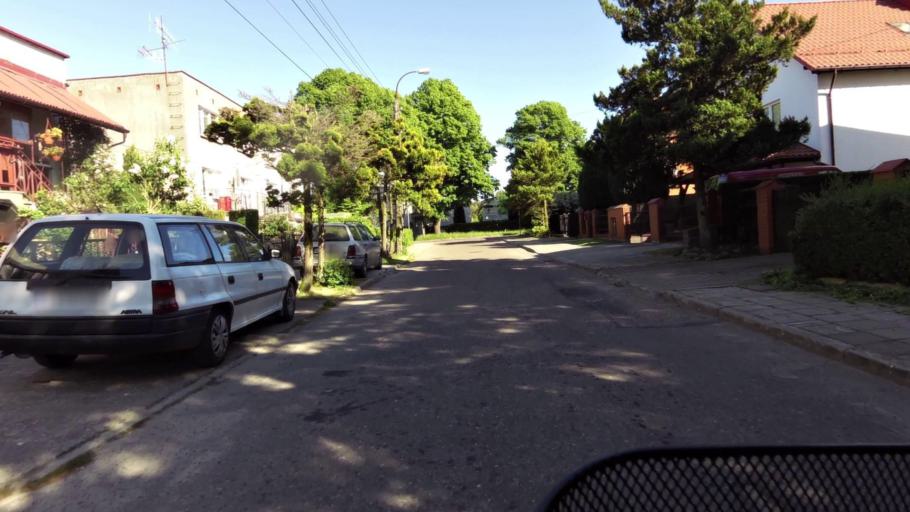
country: PL
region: West Pomeranian Voivodeship
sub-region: Koszalin
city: Koszalin
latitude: 54.1835
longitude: 16.2191
